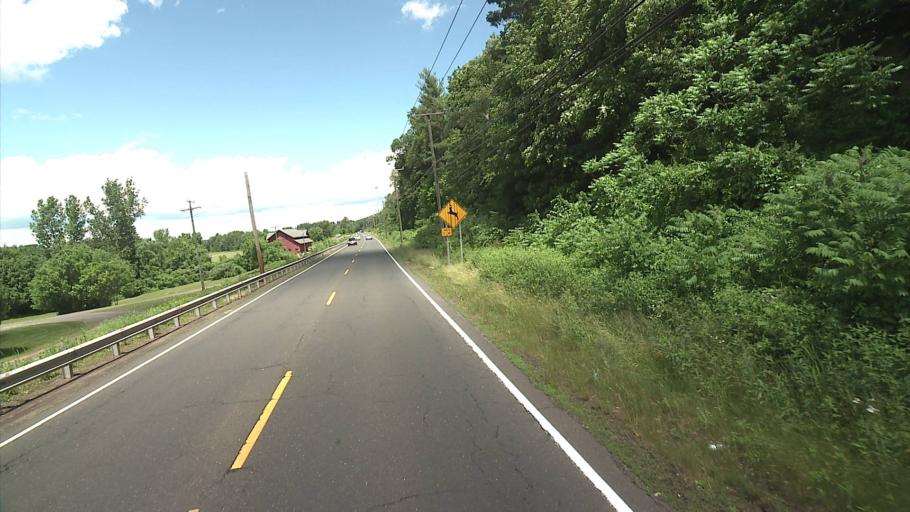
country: US
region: Connecticut
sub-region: Hartford County
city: Hazardville
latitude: 42.0199
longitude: -72.5144
